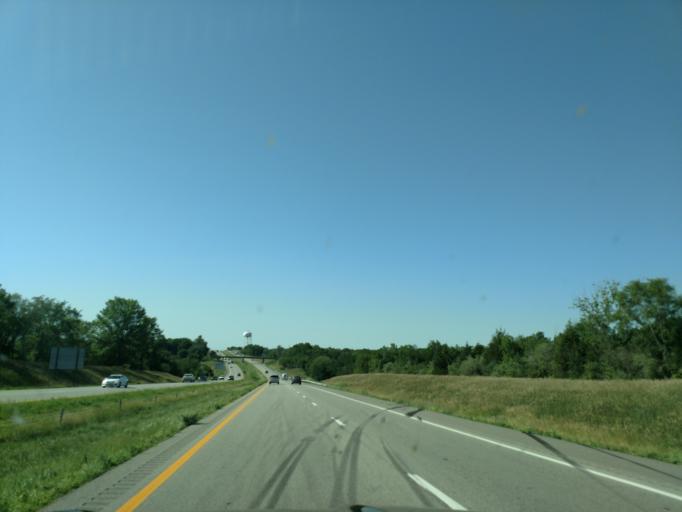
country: US
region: Missouri
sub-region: Andrew County
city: Country Club Village
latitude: 39.7870
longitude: -94.7951
